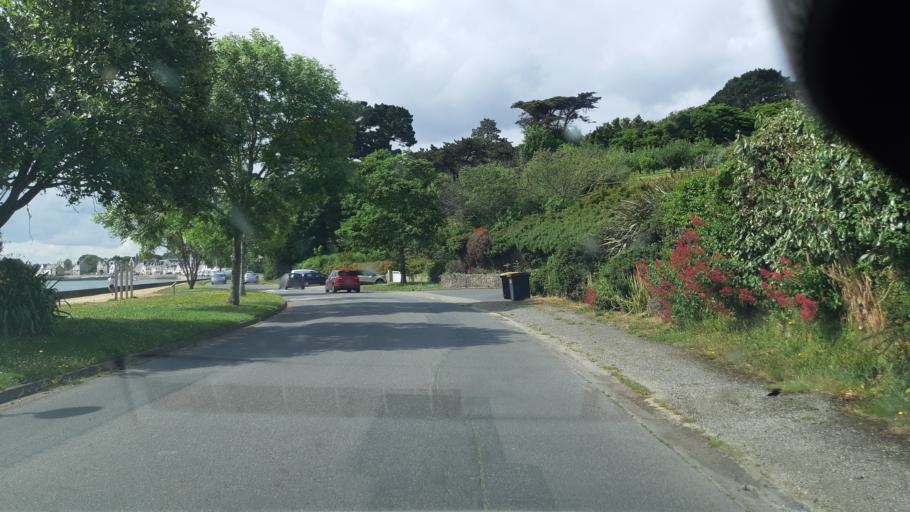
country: FR
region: Brittany
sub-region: Departement du Finistere
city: Saint-Pol-de-Leon
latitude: 48.6867
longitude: -3.9706
